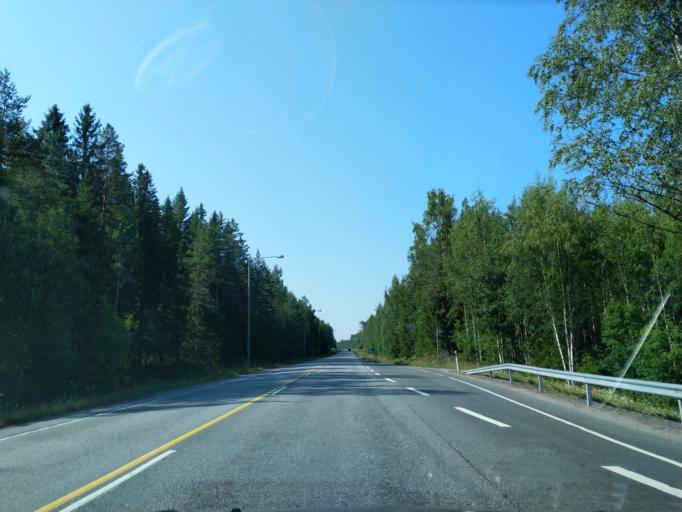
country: FI
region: Satakunta
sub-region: Pori
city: Pomarkku
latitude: 61.6897
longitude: 21.9985
